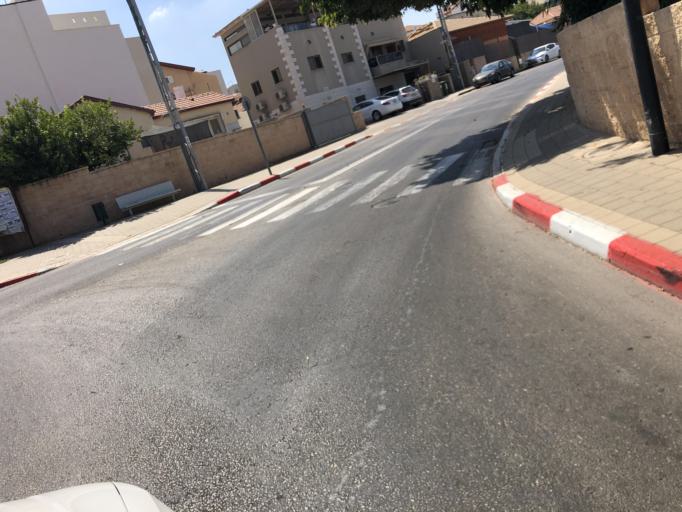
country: IL
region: Central District
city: Rosh Ha'Ayin
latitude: 32.0929
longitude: 34.9580
